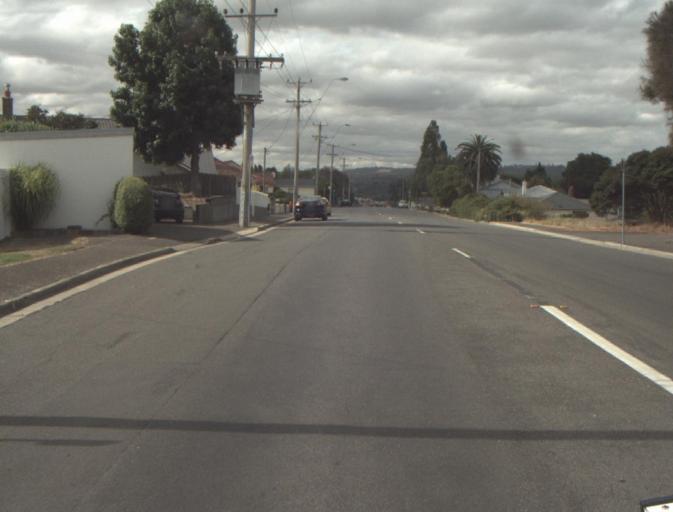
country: AU
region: Tasmania
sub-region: Launceston
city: East Launceston
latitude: -41.4526
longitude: 147.1542
